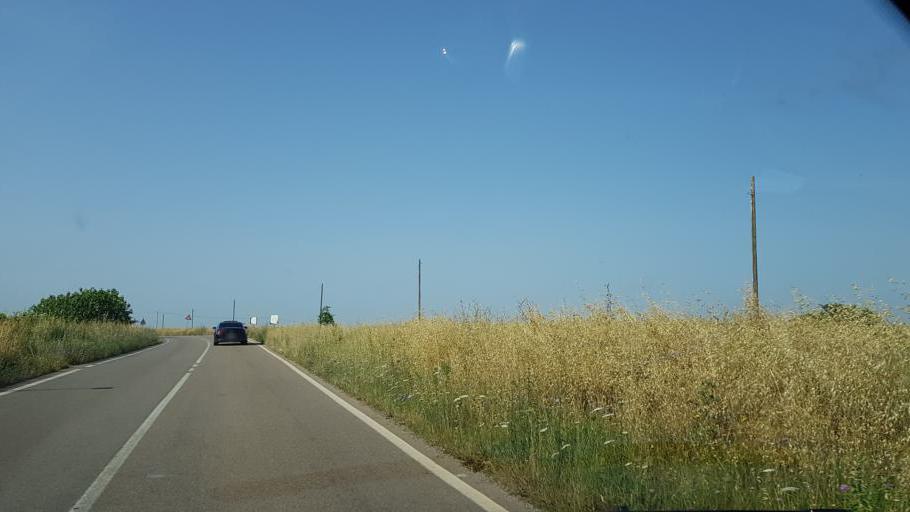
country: IT
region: Apulia
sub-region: Provincia di Brindisi
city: San Pancrazio Salentino
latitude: 40.4386
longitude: 17.8397
